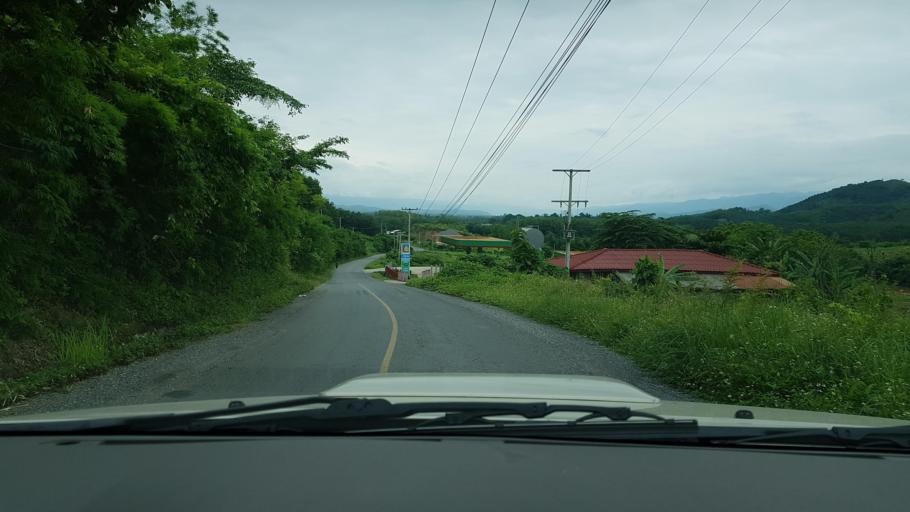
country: LA
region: Loungnamtha
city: Muang Nale
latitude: 20.1650
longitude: 101.5076
